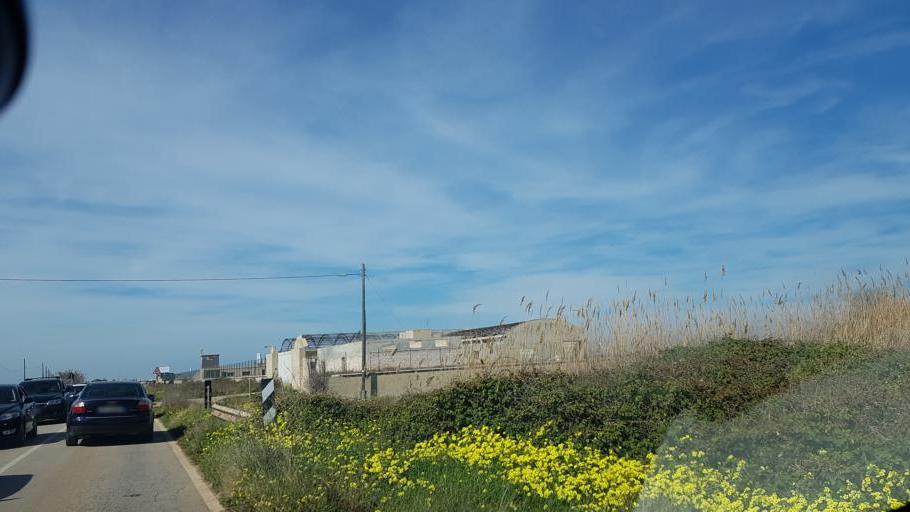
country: IT
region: Apulia
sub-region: Provincia di Brindisi
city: Pezze di Greco
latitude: 40.8593
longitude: 17.4316
